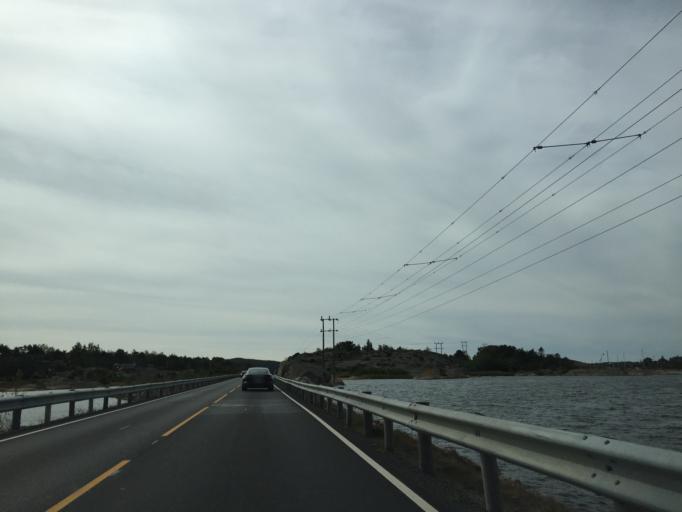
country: NO
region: Ostfold
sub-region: Fredrikstad
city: Fredrikstad
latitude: 59.1295
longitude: 10.9250
